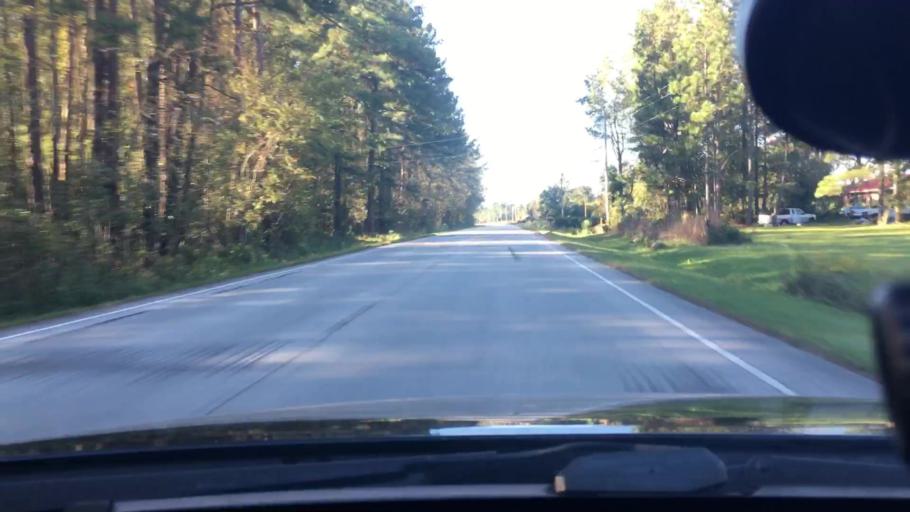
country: US
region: North Carolina
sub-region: Craven County
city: Vanceboro
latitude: 35.3973
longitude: -77.2355
